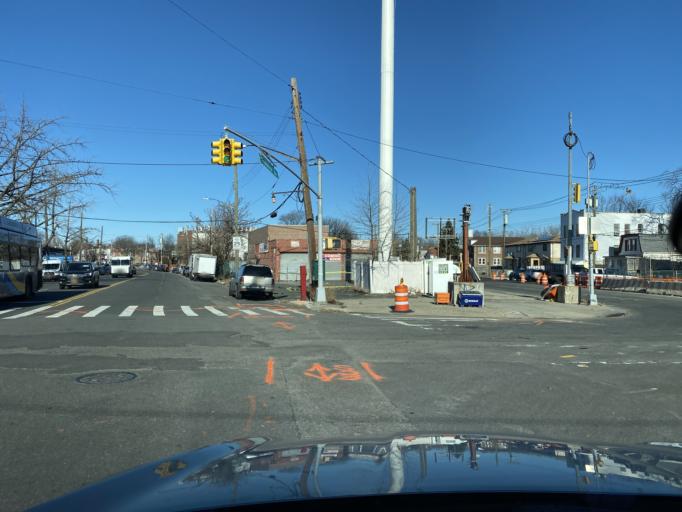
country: US
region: New York
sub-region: Bronx
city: The Bronx
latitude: 40.8114
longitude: -73.8561
